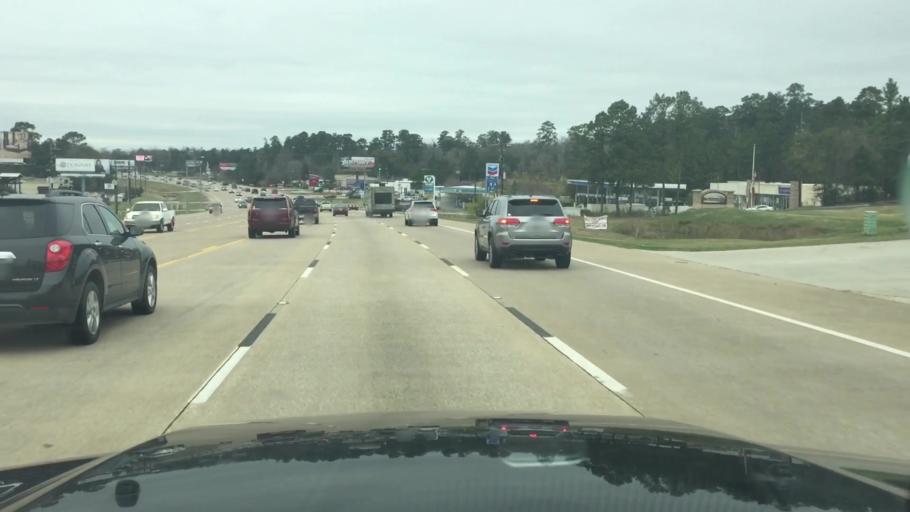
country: US
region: Texas
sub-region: Montgomery County
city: Panorama Village
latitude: 30.3390
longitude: -95.5197
